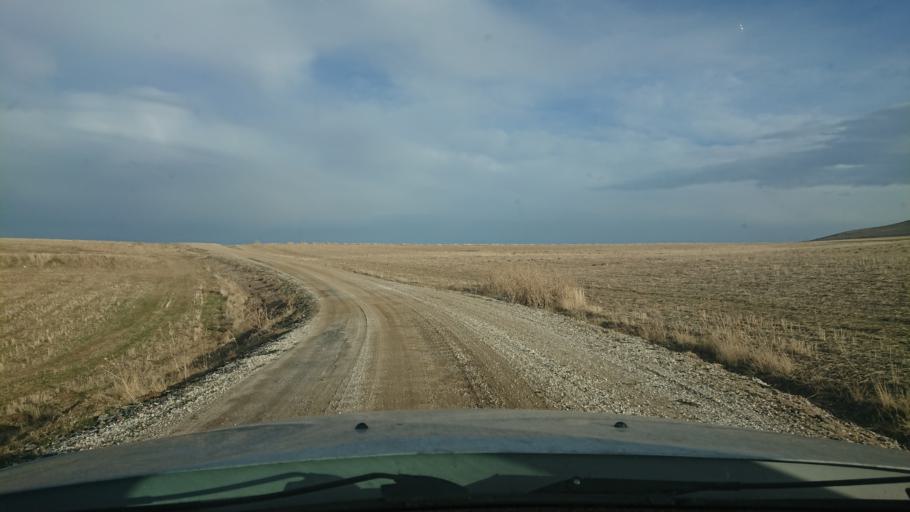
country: TR
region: Aksaray
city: Ortakoy
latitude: 38.7023
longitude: 33.8732
